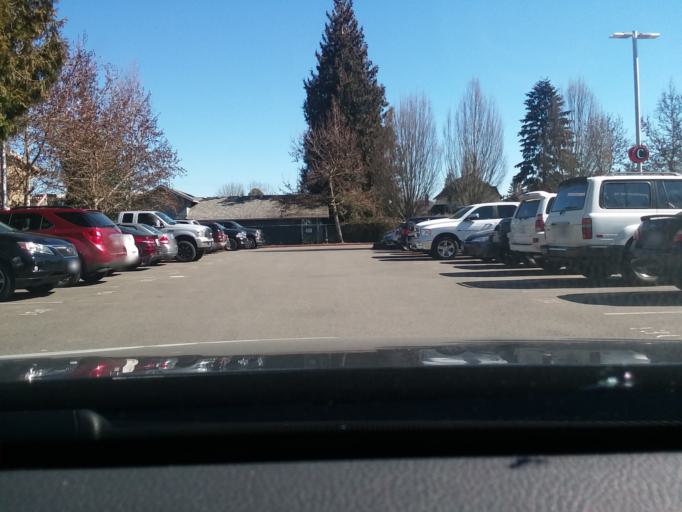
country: US
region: Washington
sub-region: Pierce County
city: Sumner
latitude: 47.2005
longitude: -122.2445
